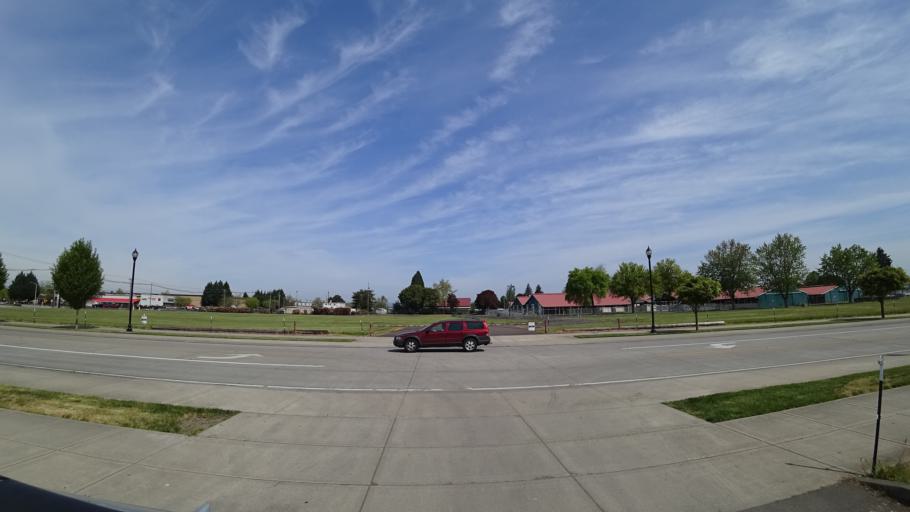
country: US
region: Oregon
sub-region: Washington County
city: Hillsboro
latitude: 45.5278
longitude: -122.9525
